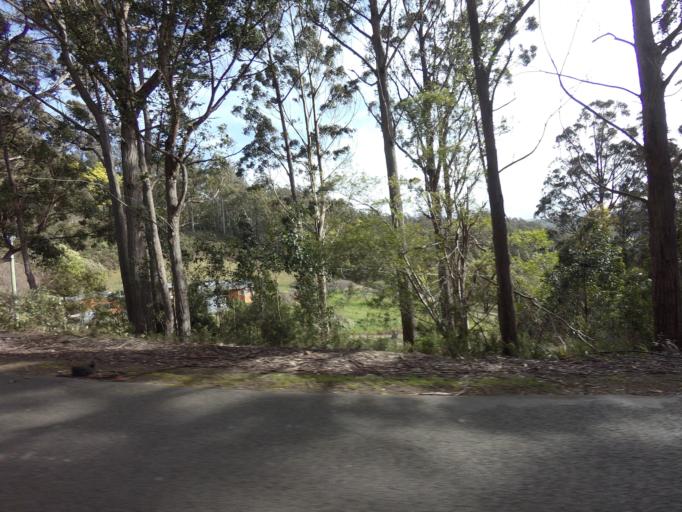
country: AU
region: Tasmania
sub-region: Kingborough
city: Margate
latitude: -43.0092
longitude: 147.1671
